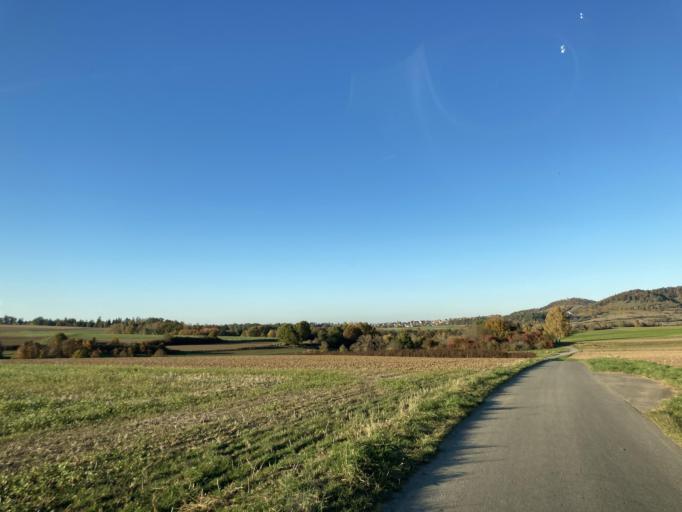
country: DE
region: Baden-Wuerttemberg
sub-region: Tuebingen Region
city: Hirrlingen
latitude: 48.4274
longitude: 8.9181
